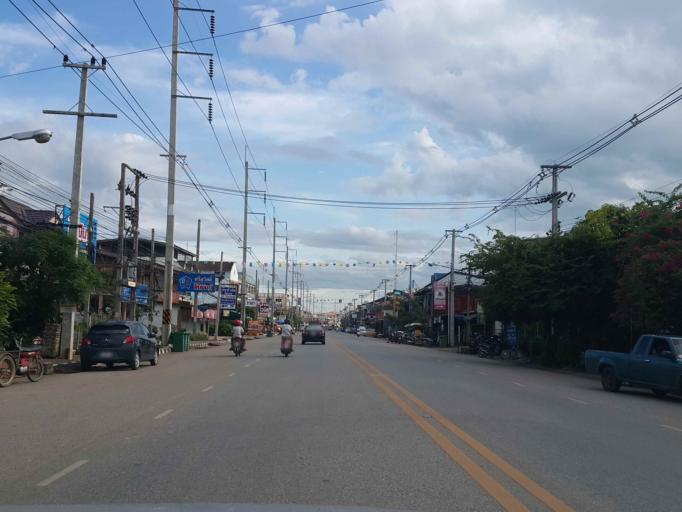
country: TH
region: Sukhothai
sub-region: Amphoe Si Satchanalai
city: Si Satchanalai
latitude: 17.5238
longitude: 99.7655
